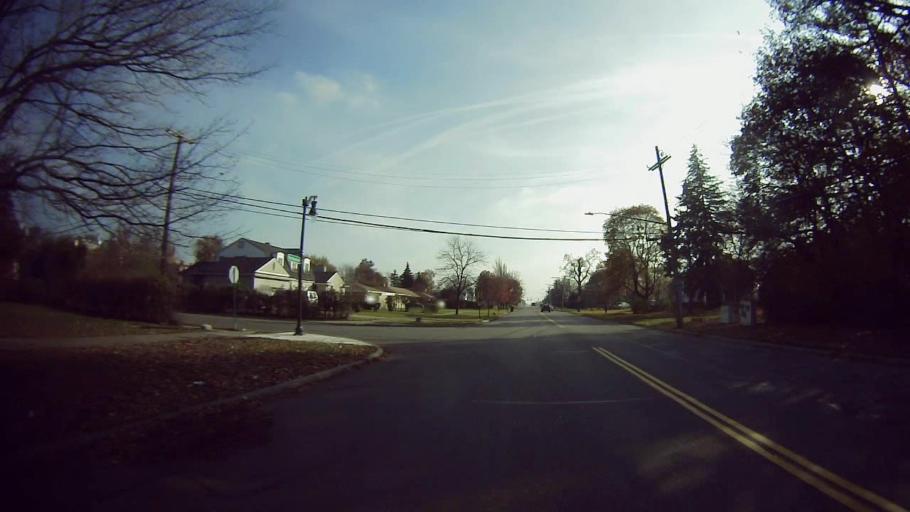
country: US
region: Michigan
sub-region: Wayne County
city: Highland Park
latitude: 42.4205
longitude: -83.1184
